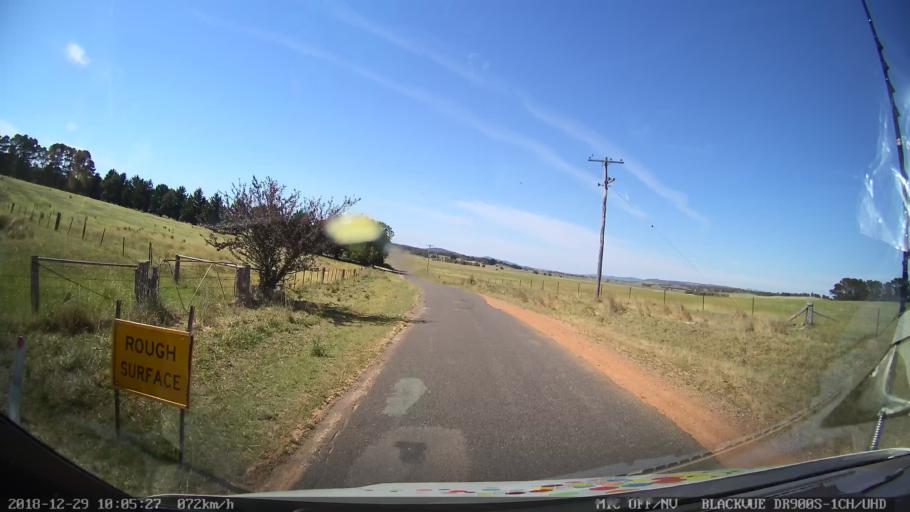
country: AU
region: New South Wales
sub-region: Goulburn Mulwaree
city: Goulburn
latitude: -34.8333
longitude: 149.4530
